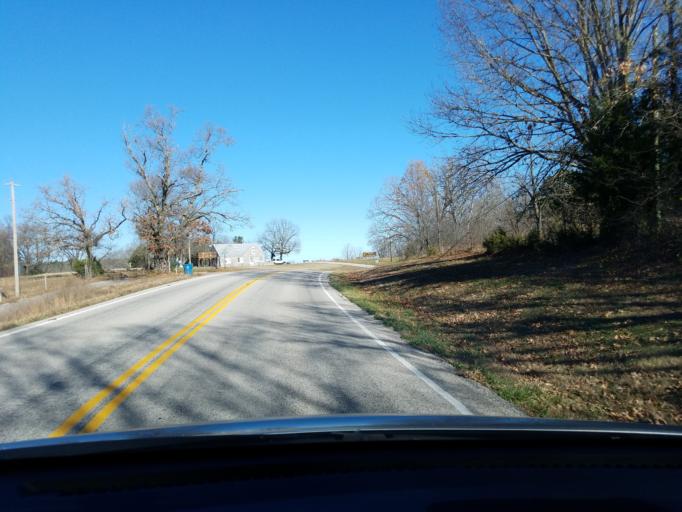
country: US
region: Missouri
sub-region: Stone County
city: Kimberling City
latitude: 36.5375
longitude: -93.3921
